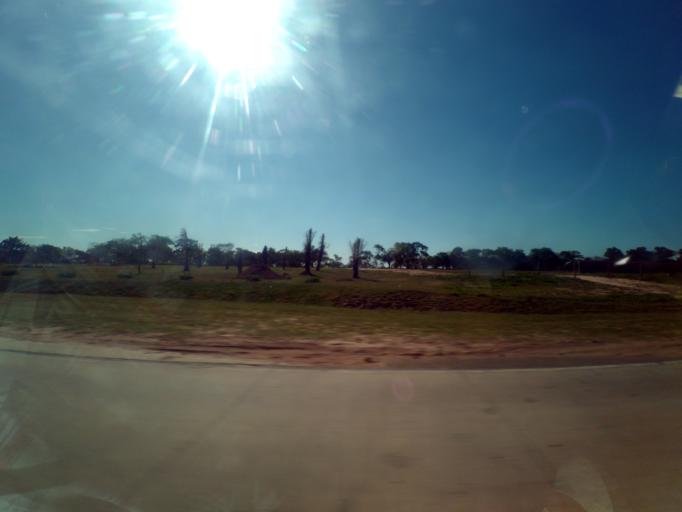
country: BO
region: Santa Cruz
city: Santa Cruz de la Sierra
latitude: -17.7768
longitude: -63.2477
